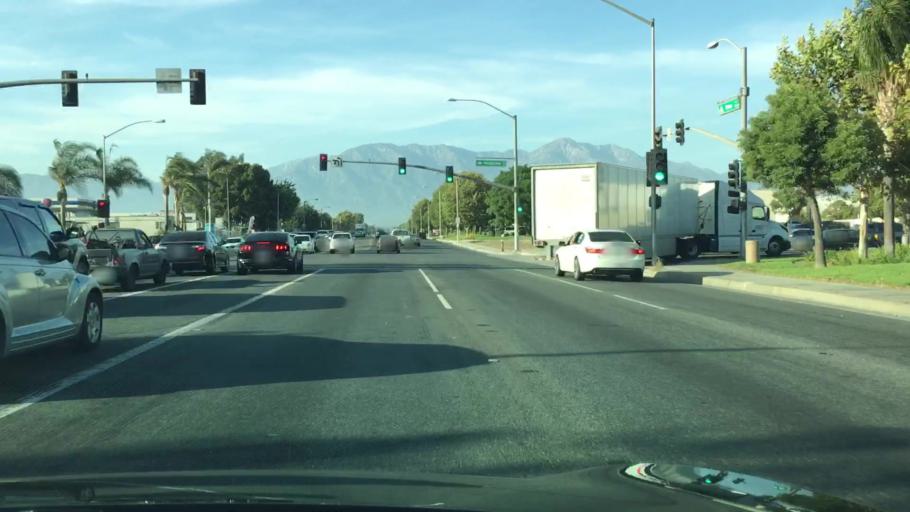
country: US
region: California
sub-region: San Bernardino County
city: Ontario
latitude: 34.0336
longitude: -117.6284
